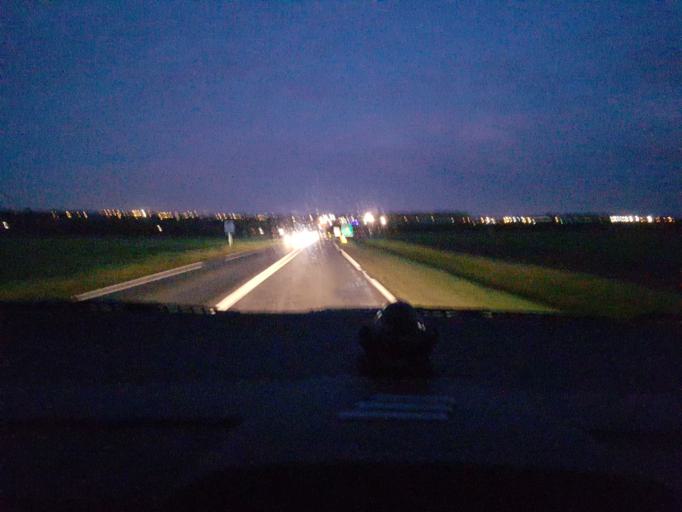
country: FR
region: Nord-Pas-de-Calais
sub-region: Departement du Pas-de-Calais
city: Dainville
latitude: 50.2670
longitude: 2.7072
